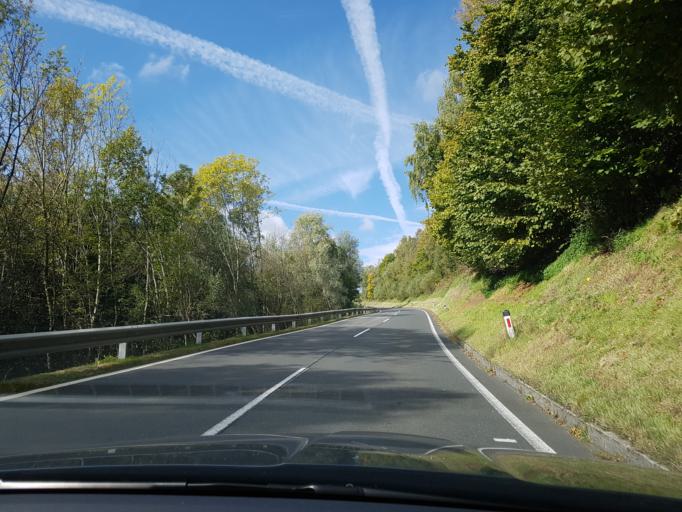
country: AT
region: Carinthia
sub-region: Politischer Bezirk Feldkirchen
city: Himmelberg
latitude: 46.7701
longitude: 14.0105
